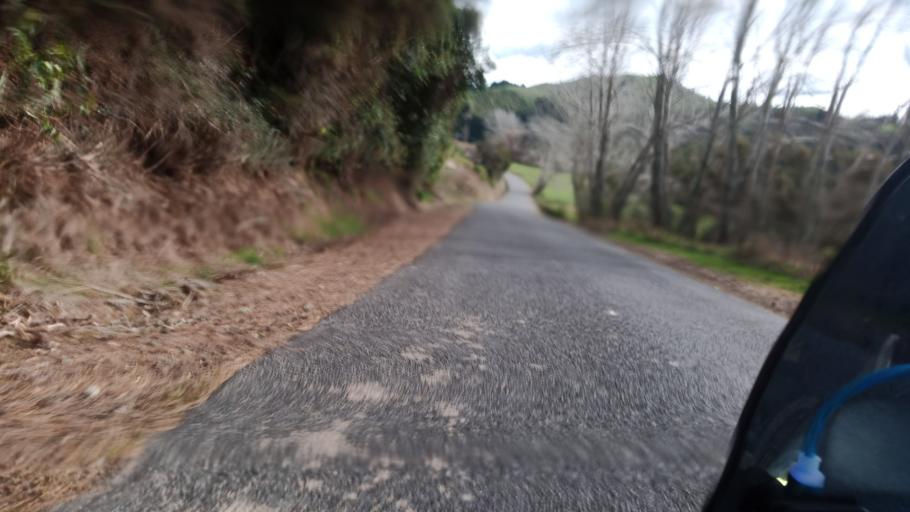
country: NZ
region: Hawke's Bay
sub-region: Wairoa District
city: Wairoa
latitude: -38.8004
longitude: 177.4691
